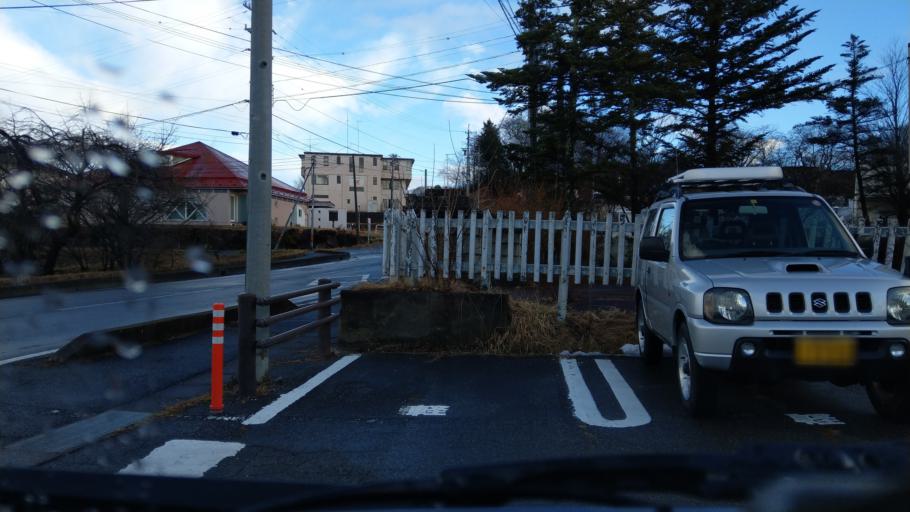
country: JP
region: Nagano
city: Kamimaruko
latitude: 36.2716
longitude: 138.3155
